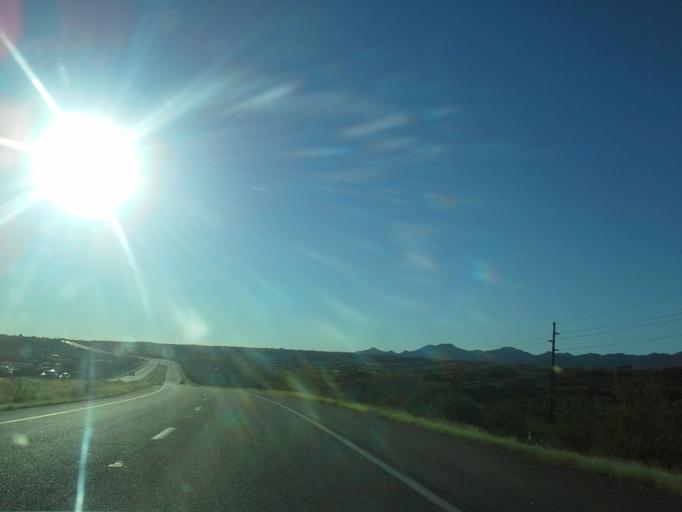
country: US
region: Arizona
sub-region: Pima County
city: Oro Valley
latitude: 32.4272
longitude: -110.9358
